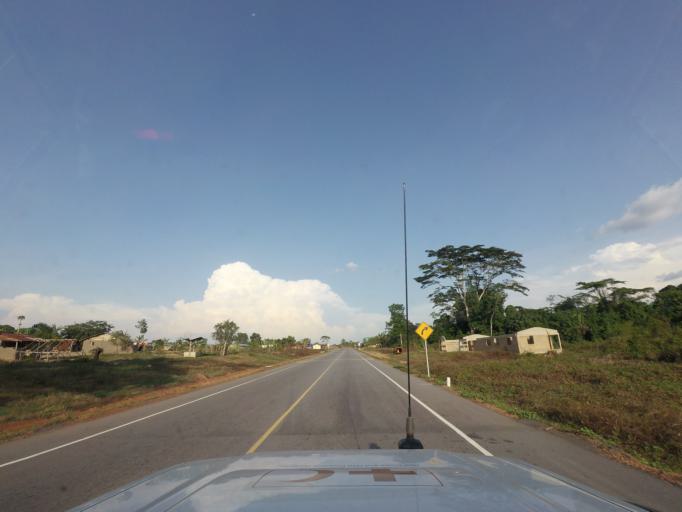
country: LR
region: Bong
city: Gbarnga
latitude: 7.0094
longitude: -9.3536
